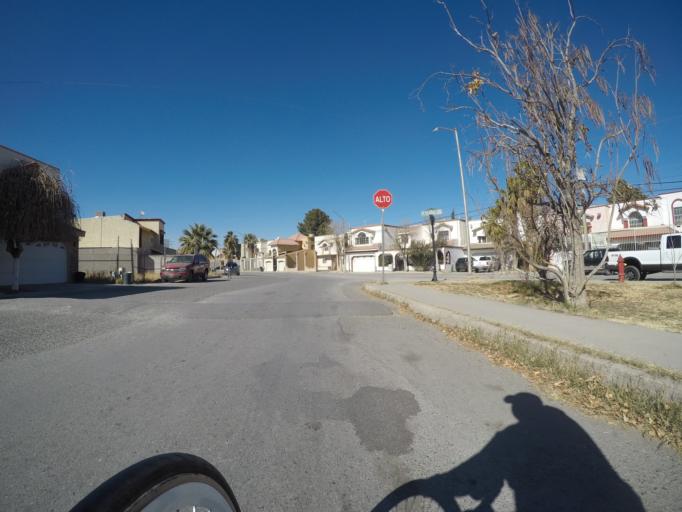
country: MX
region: Chihuahua
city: Ciudad Juarez
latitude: 31.7059
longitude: -106.4132
